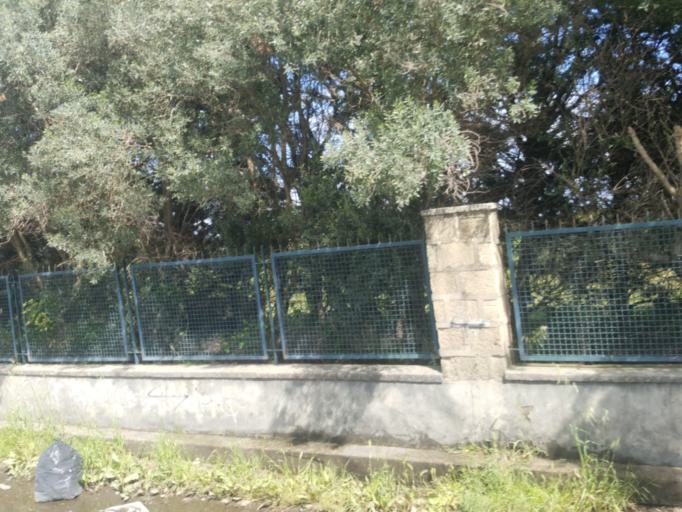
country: IT
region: Campania
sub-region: Provincia di Napoli
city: Masseria Vecchia Ovest
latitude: 40.9314
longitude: 14.0797
